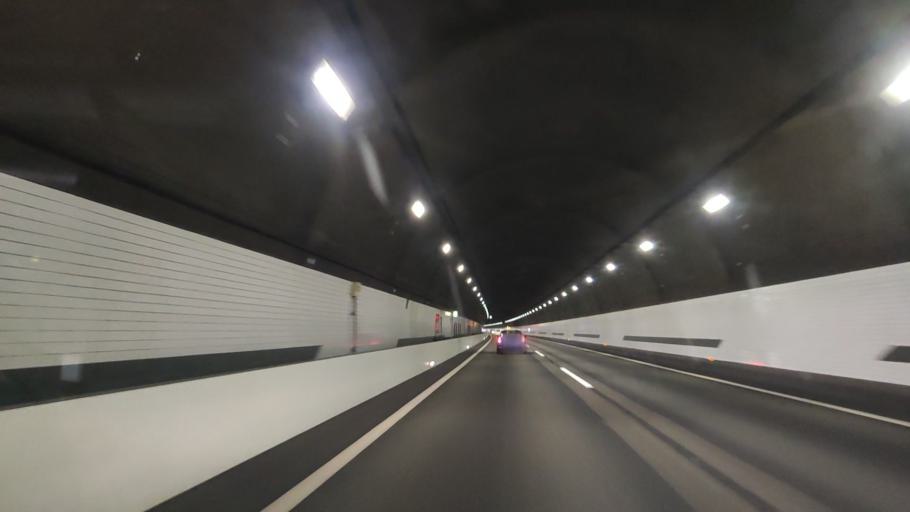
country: JP
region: Tokushima
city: Ishii
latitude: 34.1911
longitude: 134.4369
